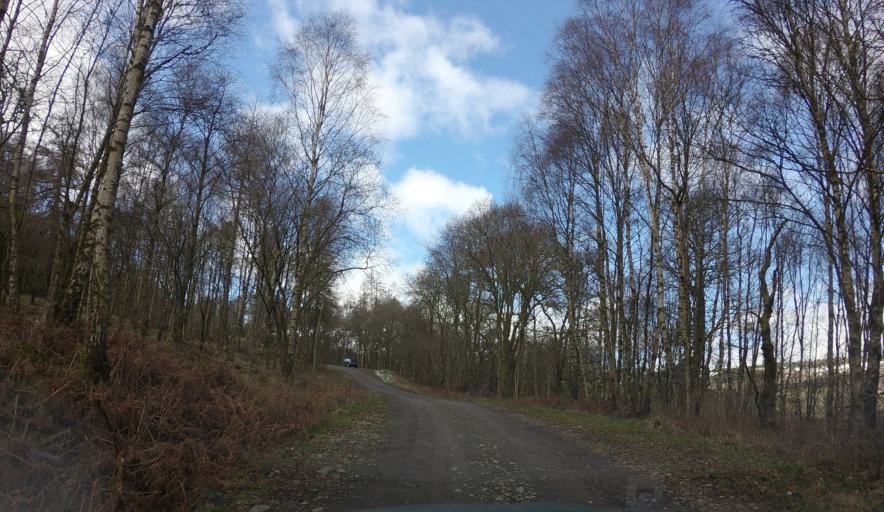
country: GB
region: Scotland
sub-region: Perth and Kinross
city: Pitlochry
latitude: 56.6508
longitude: -3.7407
